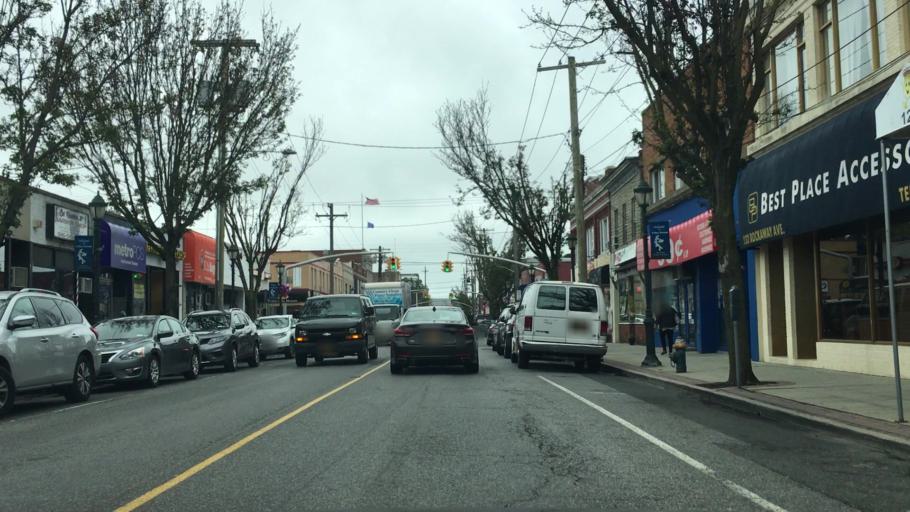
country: US
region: New York
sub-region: Nassau County
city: Valley Stream
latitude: 40.6628
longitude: -73.6990
